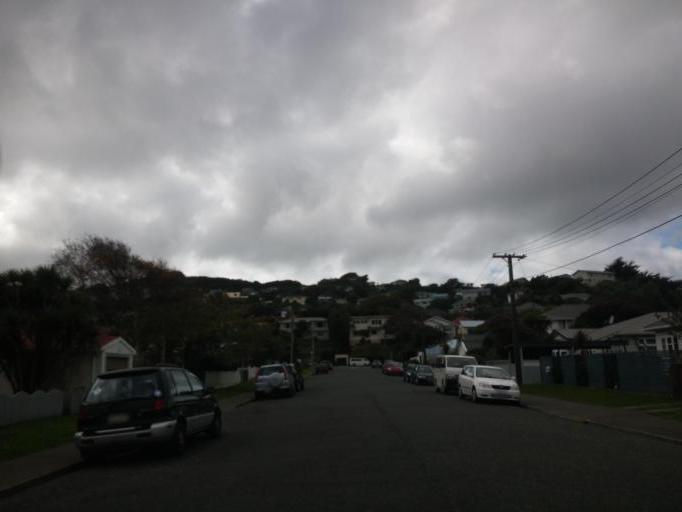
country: NZ
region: Wellington
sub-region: Wellington City
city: Brooklyn
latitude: -41.2852
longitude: 174.7255
